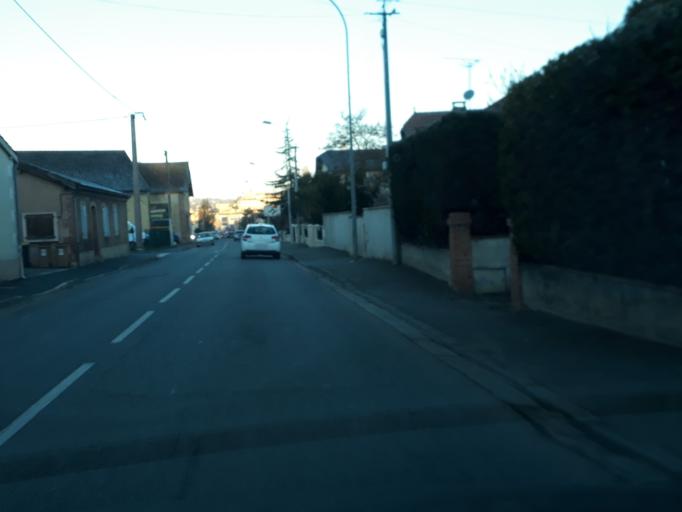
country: FR
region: Midi-Pyrenees
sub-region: Departement du Gers
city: Auch
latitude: 43.6401
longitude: 0.5981
